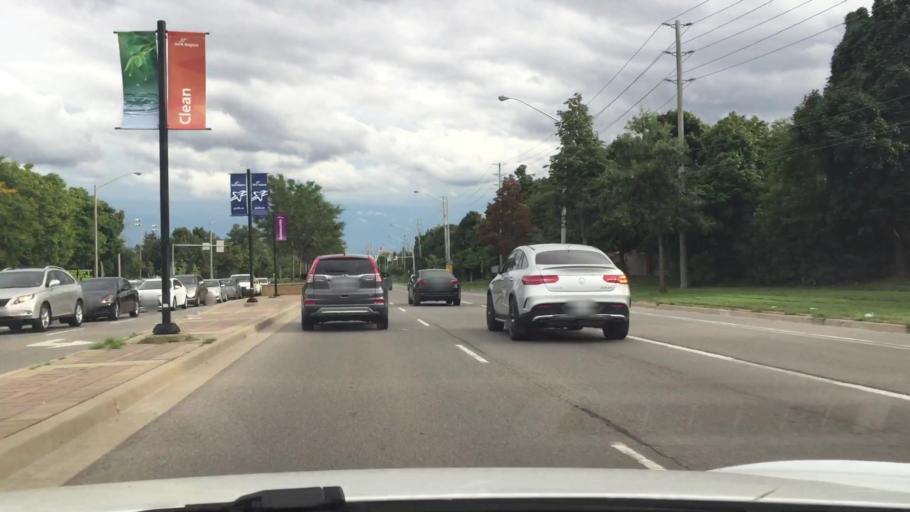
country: CA
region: Ontario
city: Concord
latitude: 43.7968
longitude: -79.4724
